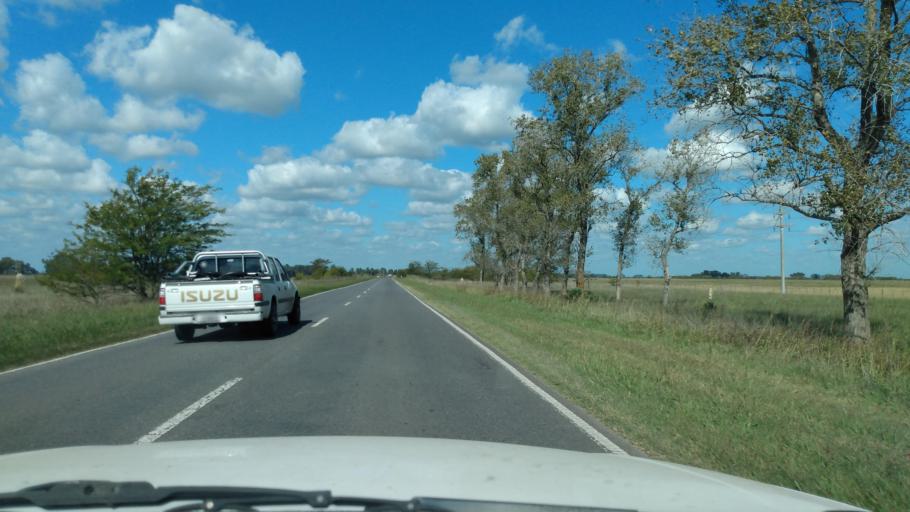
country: AR
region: Buenos Aires
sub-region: Partido de Navarro
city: Navarro
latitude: -34.8704
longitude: -59.3421
